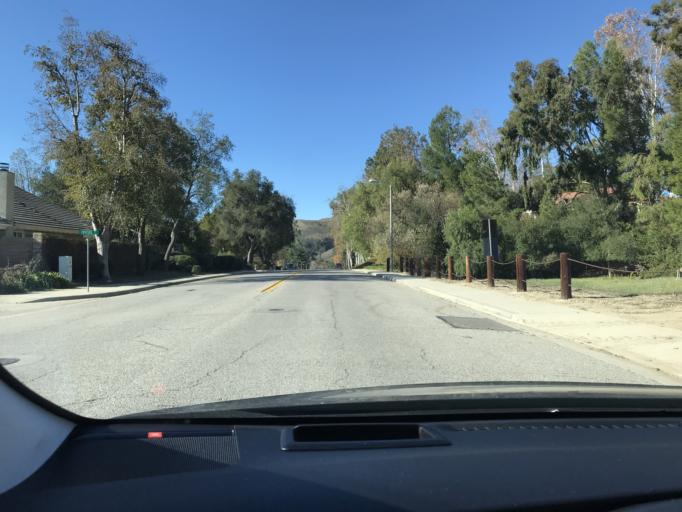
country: US
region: California
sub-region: Ventura County
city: Oak Park
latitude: 34.1774
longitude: -118.7559
